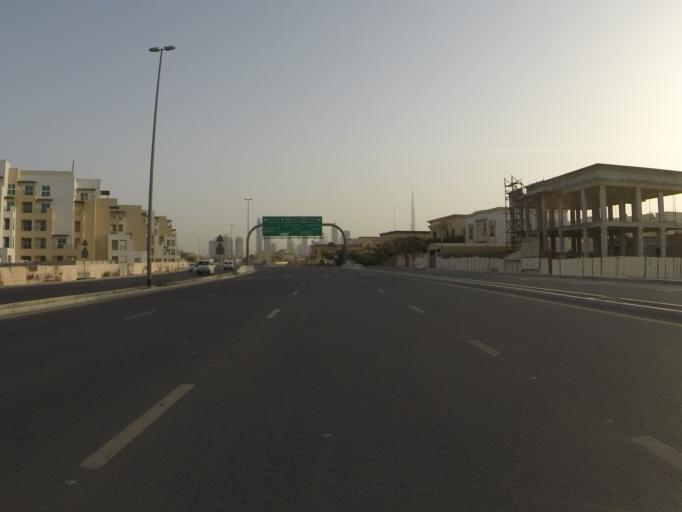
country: AE
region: Dubai
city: Dubai
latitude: 25.1557
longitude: 55.2569
